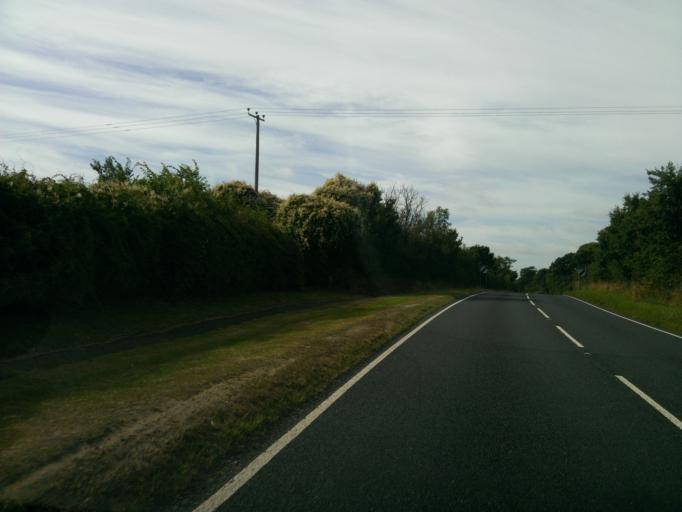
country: GB
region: England
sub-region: Essex
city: Saint Osyth
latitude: 51.8131
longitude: 1.0745
